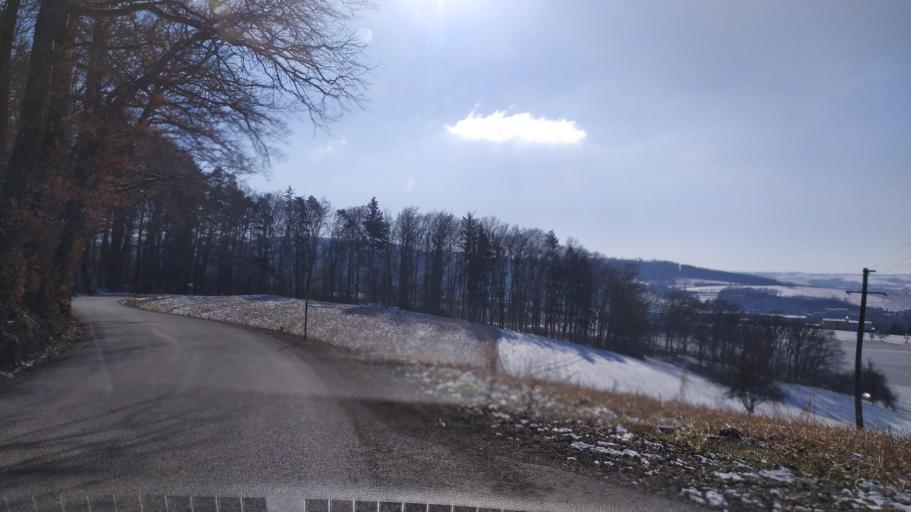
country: AT
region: Upper Austria
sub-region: Politischer Bezirk Urfahr-Umgebung
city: Ottensheim
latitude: 48.3415
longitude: 14.1933
